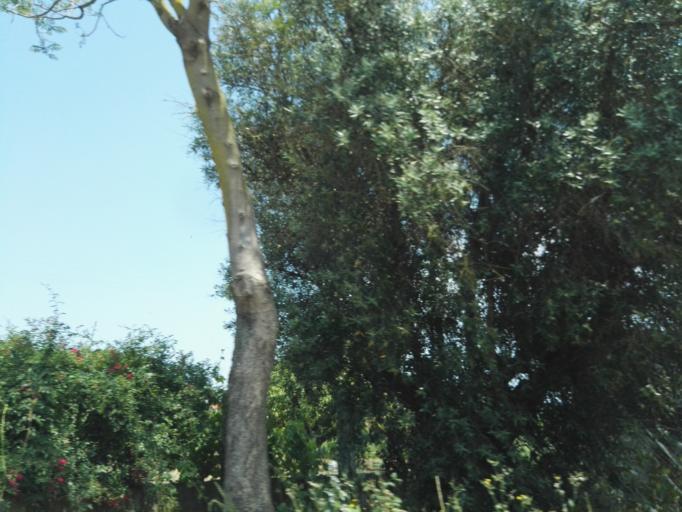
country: PT
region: Santarem
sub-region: Golega
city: Golega
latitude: 39.4071
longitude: -8.4778
